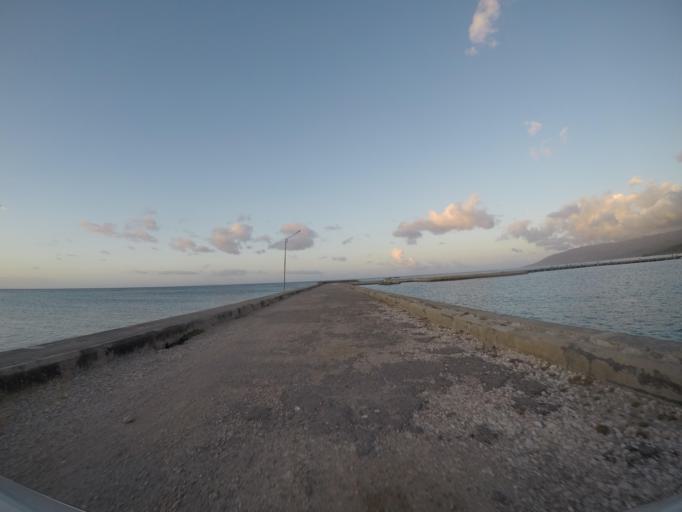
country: TL
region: Lautem
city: Lospalos
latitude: -8.3612
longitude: 127.0629
